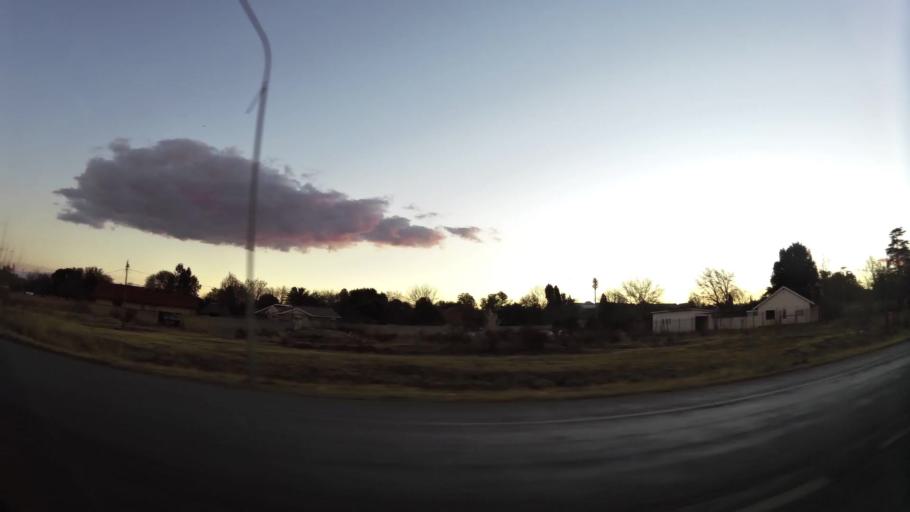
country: ZA
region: North-West
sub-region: Dr Kenneth Kaunda District Municipality
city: Potchefstroom
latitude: -26.6950
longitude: 27.0790
